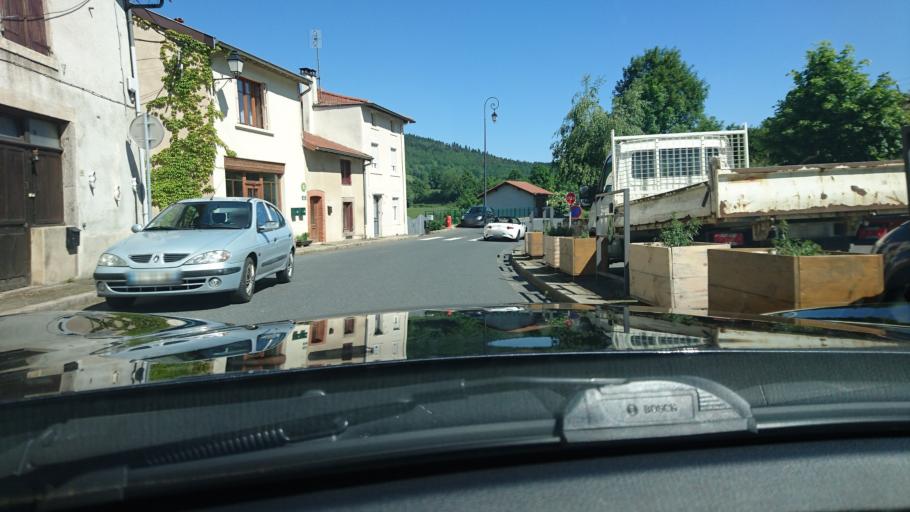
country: FR
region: Rhone-Alpes
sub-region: Departement de la Loire
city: Violay
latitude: 45.8138
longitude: 4.4045
